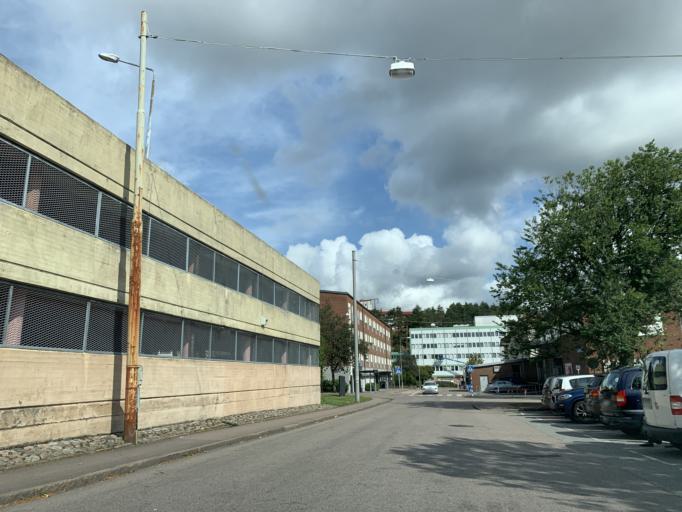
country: SE
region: Vaestra Goetaland
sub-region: Goteborg
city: Eriksbo
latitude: 57.7516
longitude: 12.0307
